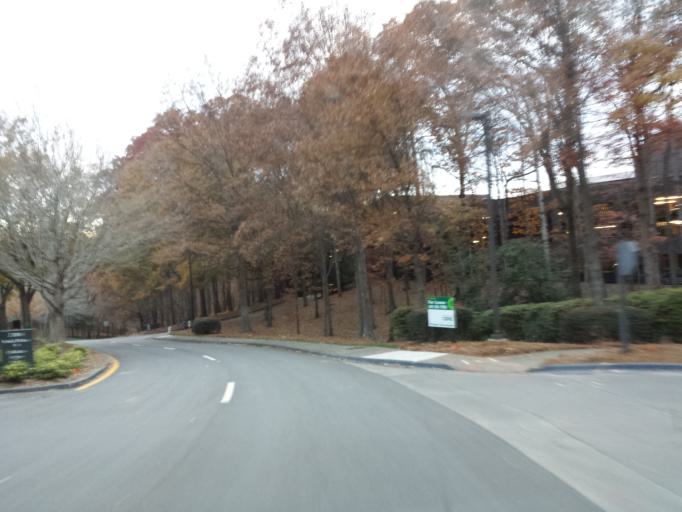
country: US
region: Georgia
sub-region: Cobb County
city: Vinings
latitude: 33.9048
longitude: -84.4594
